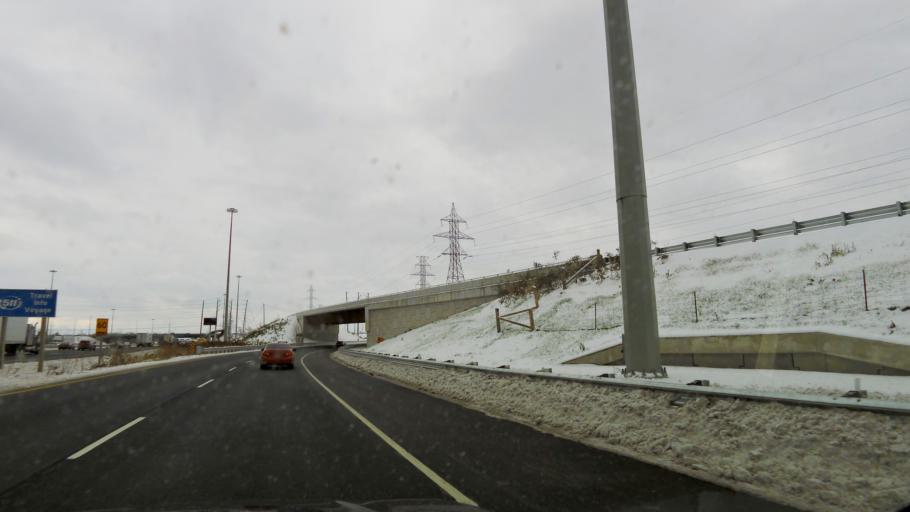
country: CA
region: Ontario
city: Mississauga
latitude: 43.5461
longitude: -79.7067
